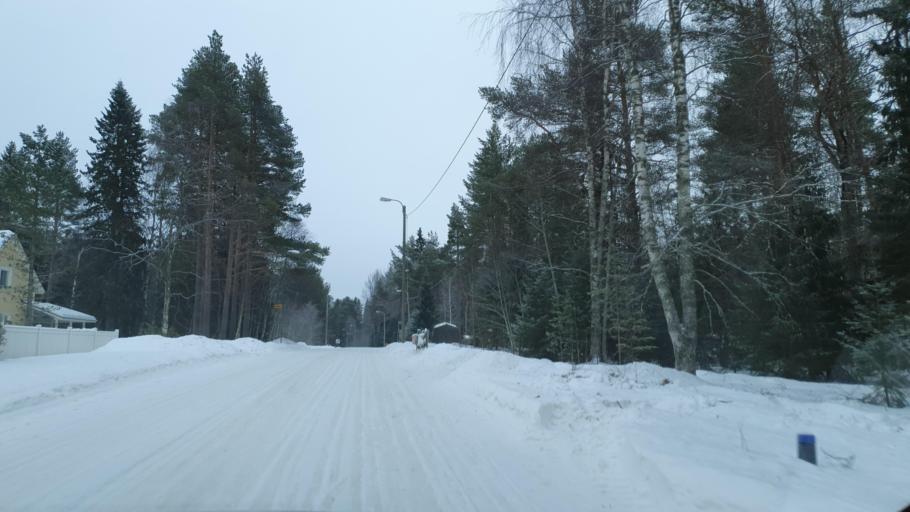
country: FI
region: Northern Ostrobothnia
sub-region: Oulu
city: Haukipudas
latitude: 65.1932
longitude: 25.4154
